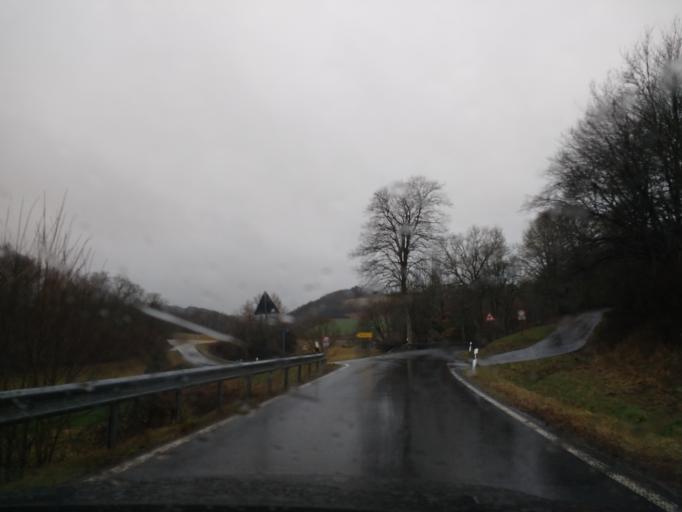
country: DE
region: Rheinland-Pfalz
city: Hilscheid
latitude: 49.7379
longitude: 6.9926
